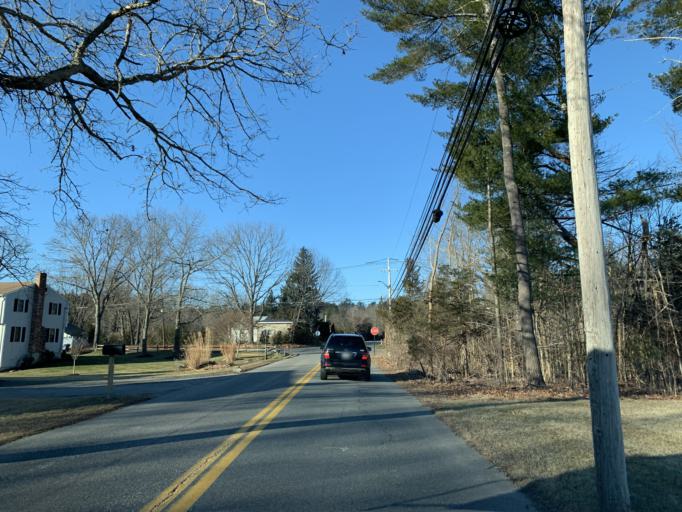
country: US
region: Massachusetts
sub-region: Essex County
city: Methuen
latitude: 42.7084
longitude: -71.2514
